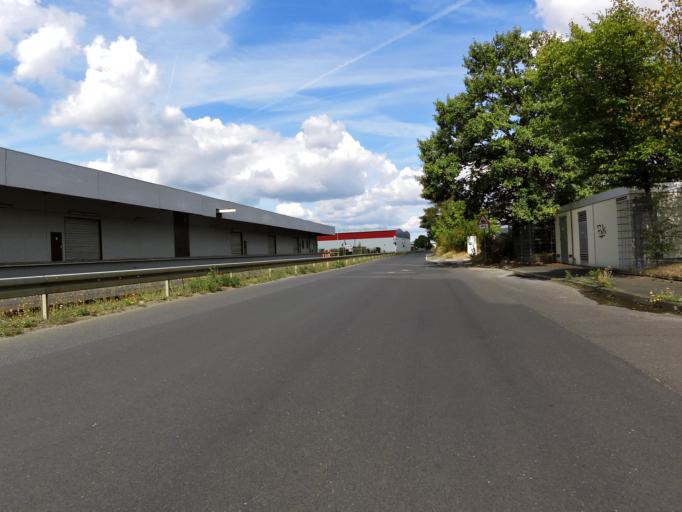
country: DE
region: Bavaria
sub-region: Regierungsbezirk Unterfranken
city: Zell am Main
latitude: 49.8119
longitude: 9.8766
